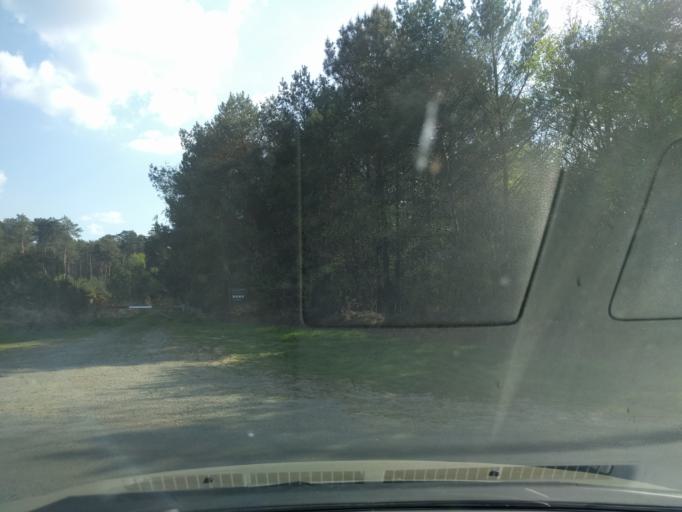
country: FR
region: Brittany
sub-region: Departement d'Ille-et-Vilaine
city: Gosne
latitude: 48.2847
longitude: -1.4597
